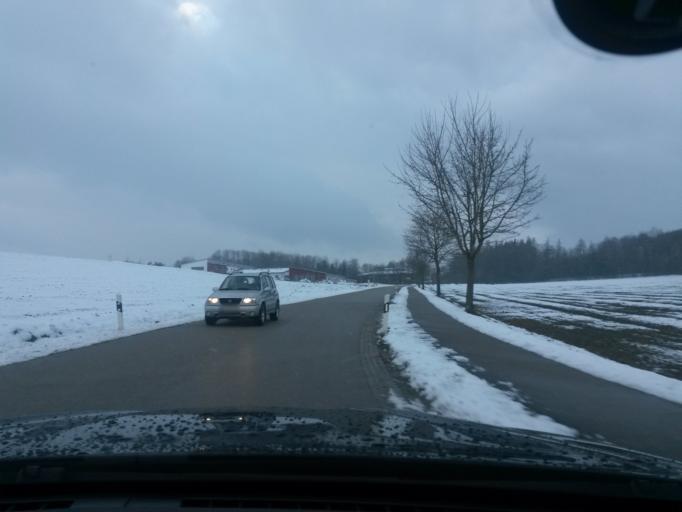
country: DE
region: Bavaria
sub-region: Lower Bavaria
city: Eching
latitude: 48.4909
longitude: 12.0512
